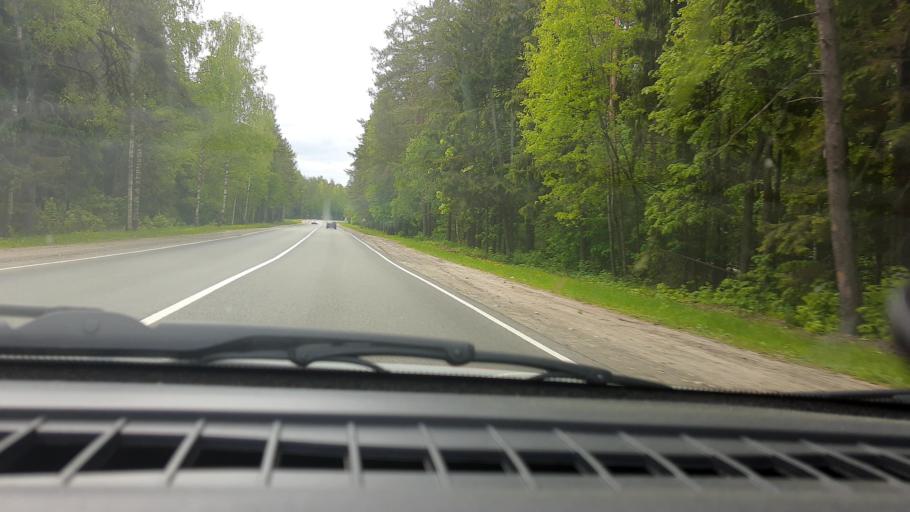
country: RU
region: Nizjnij Novgorod
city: Semenov
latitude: 56.7492
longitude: 44.3584
